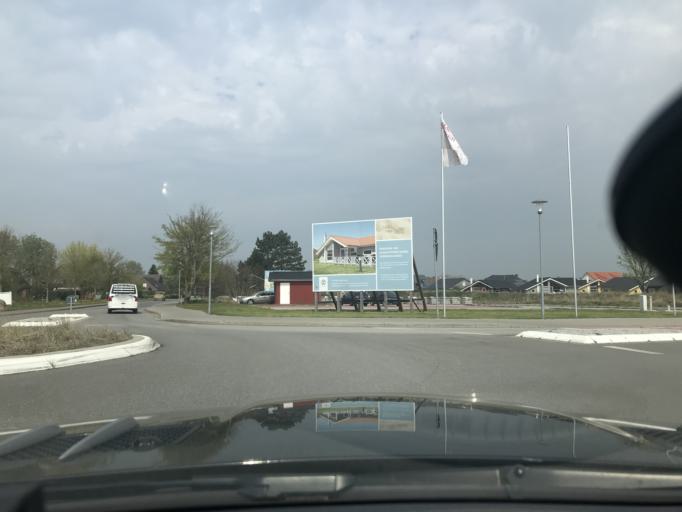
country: DE
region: Schleswig-Holstein
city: Grossenbrode
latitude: 54.3629
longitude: 11.0842
